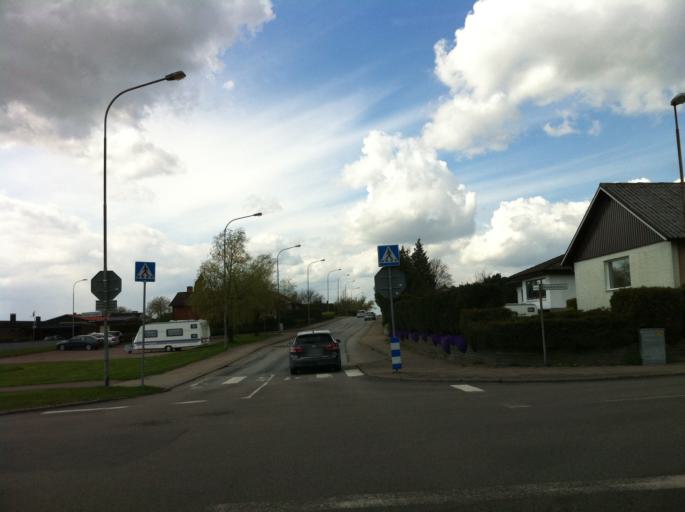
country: SE
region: Skane
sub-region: Eslovs Kommun
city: Eslov
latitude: 55.8344
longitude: 13.2853
